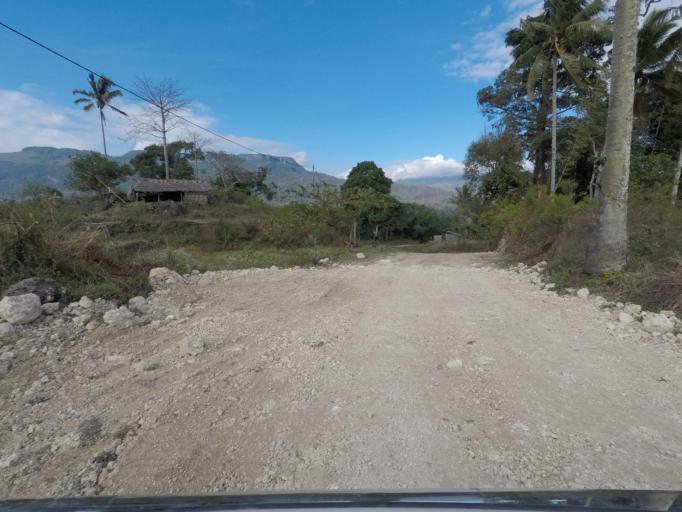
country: TL
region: Baucau
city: Venilale
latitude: -8.6476
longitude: 126.3926
